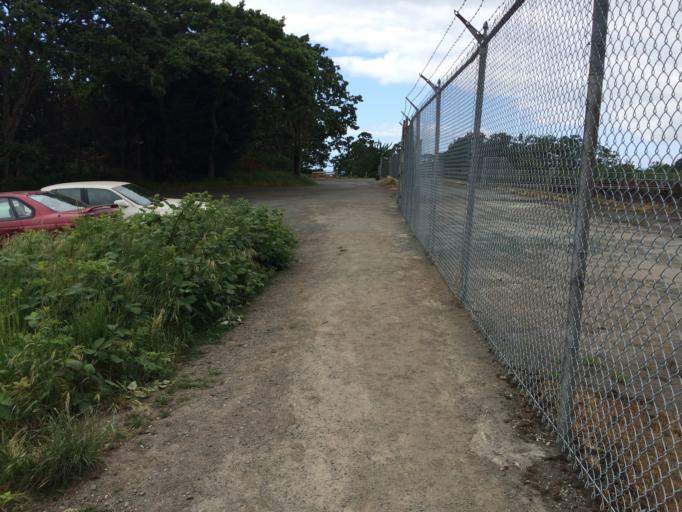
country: CA
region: British Columbia
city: Victoria
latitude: 48.4447
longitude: -123.3512
